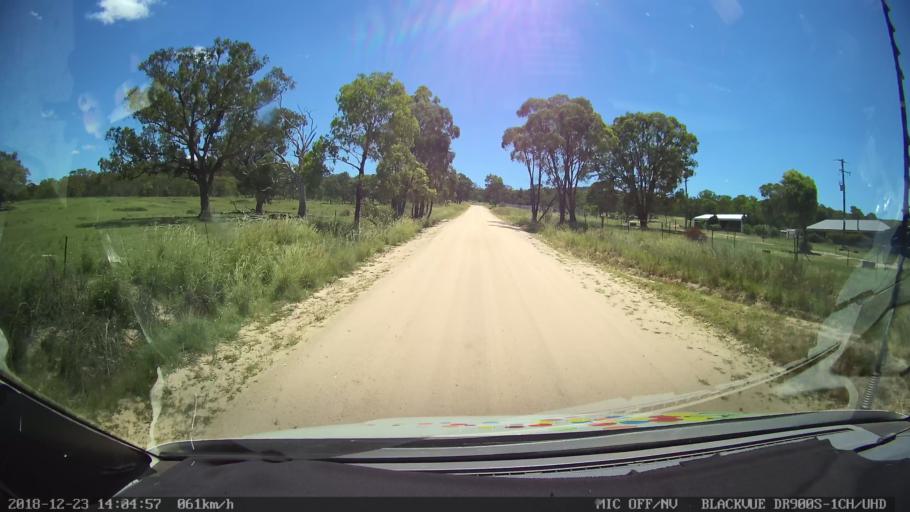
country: AU
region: New South Wales
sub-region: Tamworth Municipality
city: Manilla
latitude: -30.6236
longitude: 151.0855
